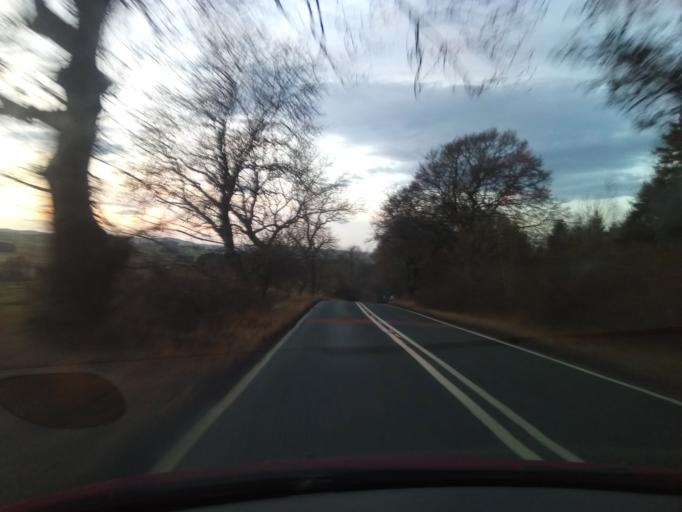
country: GB
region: England
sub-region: Northumberland
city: Otterburn
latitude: 55.2297
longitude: -2.1709
